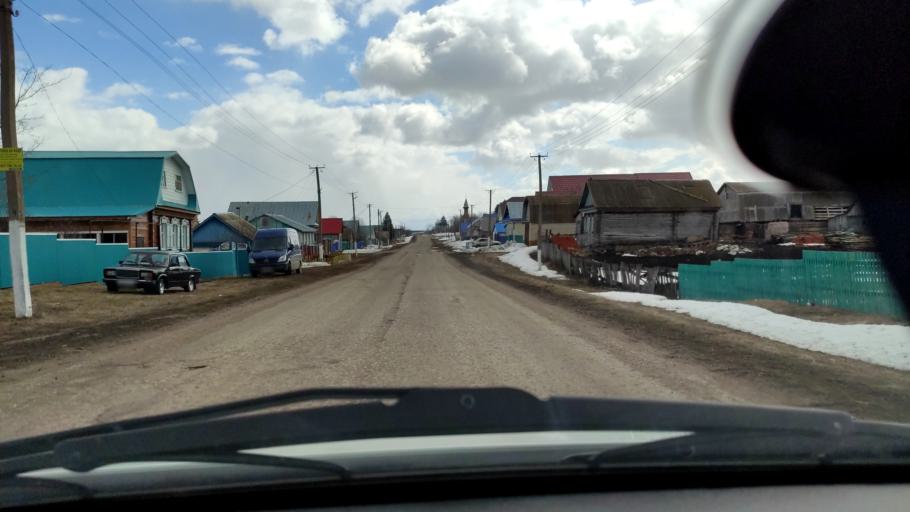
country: RU
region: Bashkortostan
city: Tolbazy
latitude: 54.1720
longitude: 55.9543
